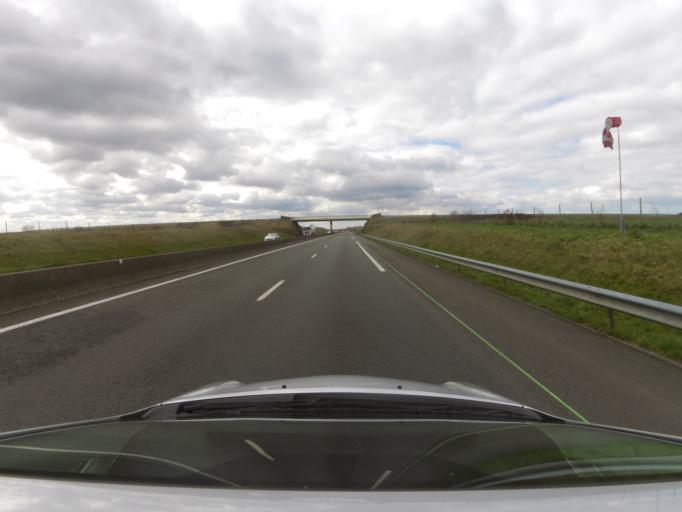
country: FR
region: Nord-Pas-de-Calais
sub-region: Departement du Pas-de-Calais
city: Verton
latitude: 50.3682
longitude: 1.6936
